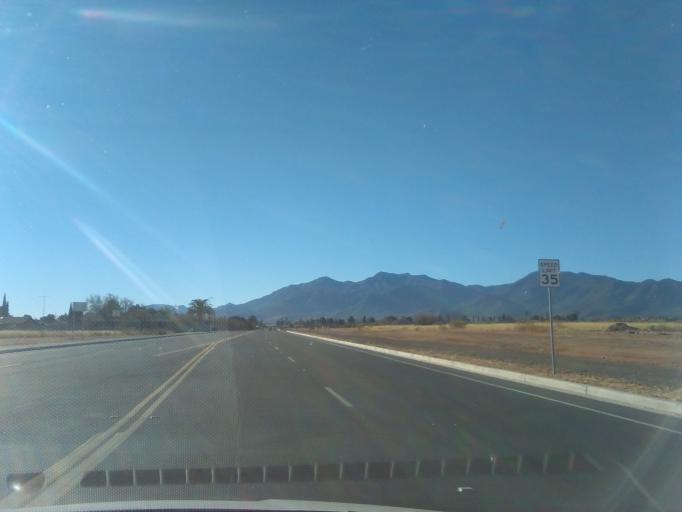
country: US
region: Arizona
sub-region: Cochise County
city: Sierra Vista
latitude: 31.5468
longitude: -110.2787
